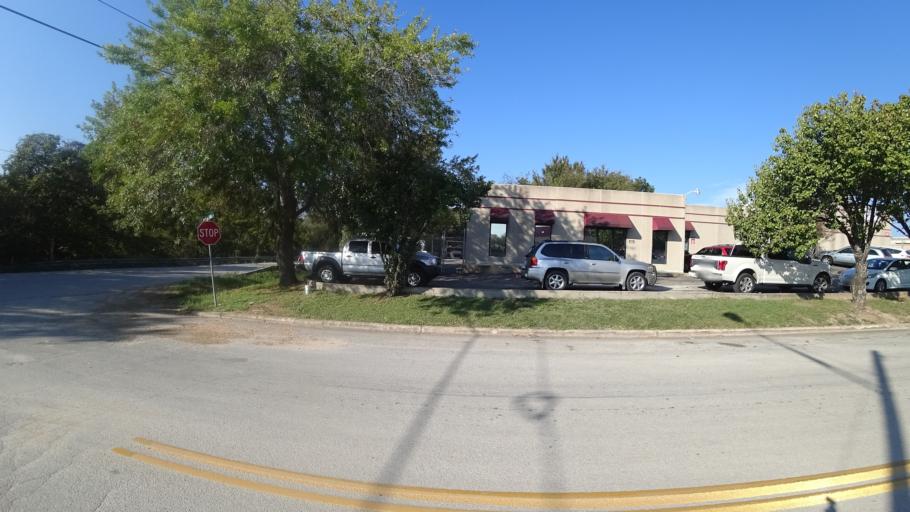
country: US
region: Texas
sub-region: Travis County
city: Manor
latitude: 30.3222
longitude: -97.6535
